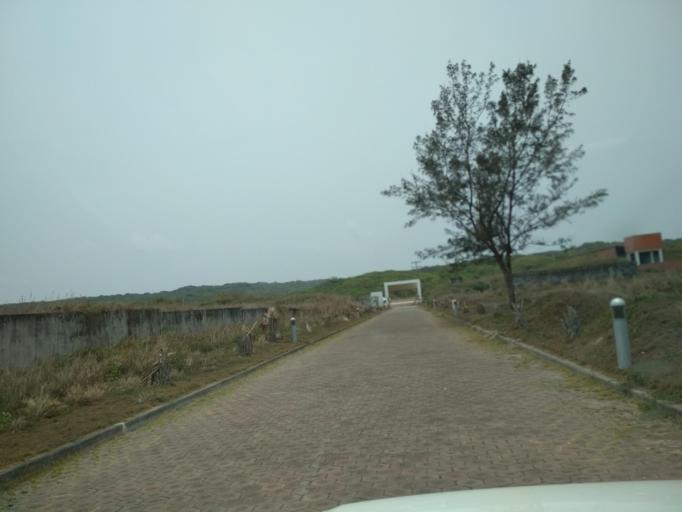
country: MX
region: Veracruz
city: Anton Lizardo
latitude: 19.0563
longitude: -96.0436
